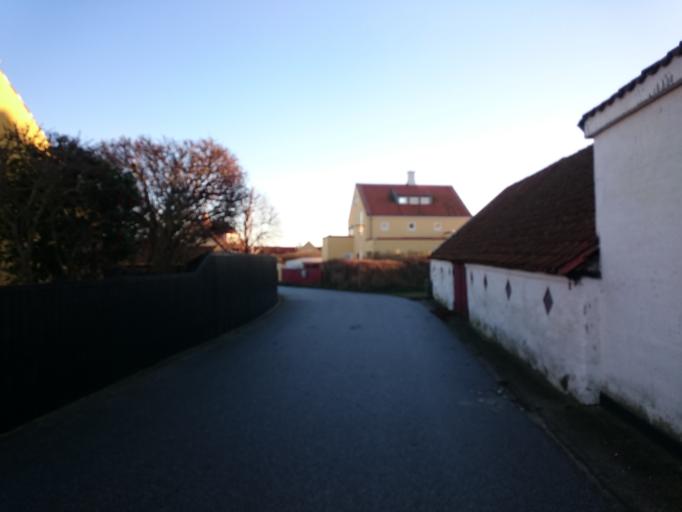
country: DK
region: North Denmark
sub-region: Frederikshavn Kommune
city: Skagen
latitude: 57.7155
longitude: 10.5739
